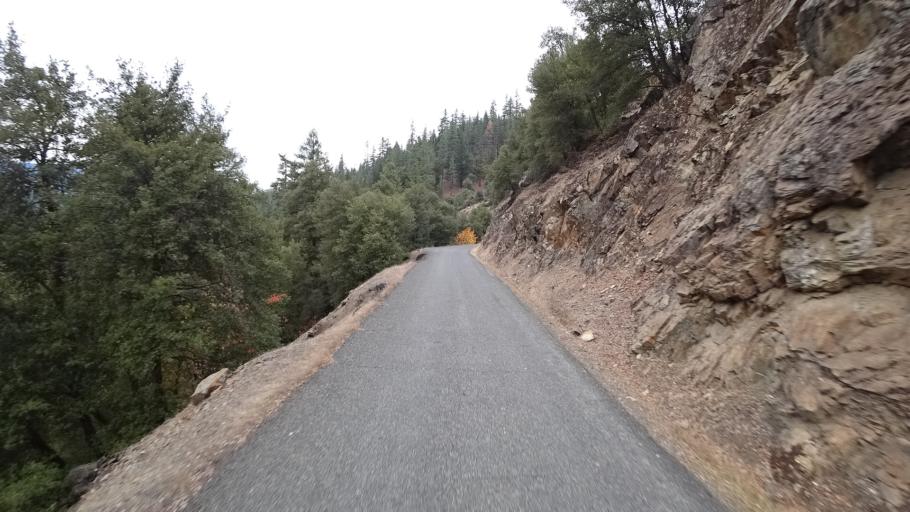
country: US
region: California
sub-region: Siskiyou County
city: Happy Camp
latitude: 41.7675
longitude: -123.3695
